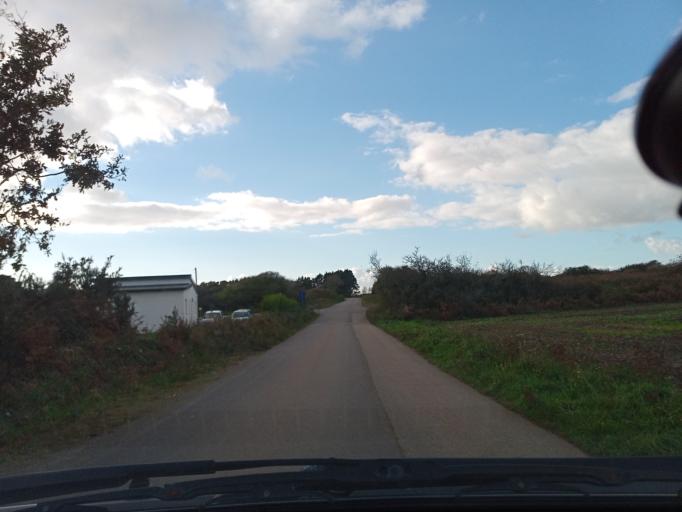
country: FR
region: Brittany
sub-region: Departement du Finistere
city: Plouhinec
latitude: 48.0173
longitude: -4.4952
